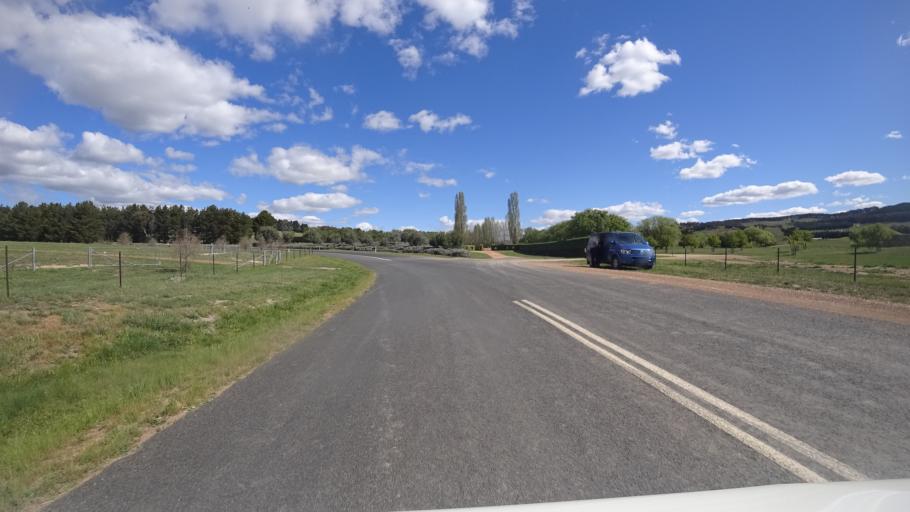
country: AU
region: New South Wales
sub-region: Oberon
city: Oberon
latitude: -33.6678
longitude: 149.7783
